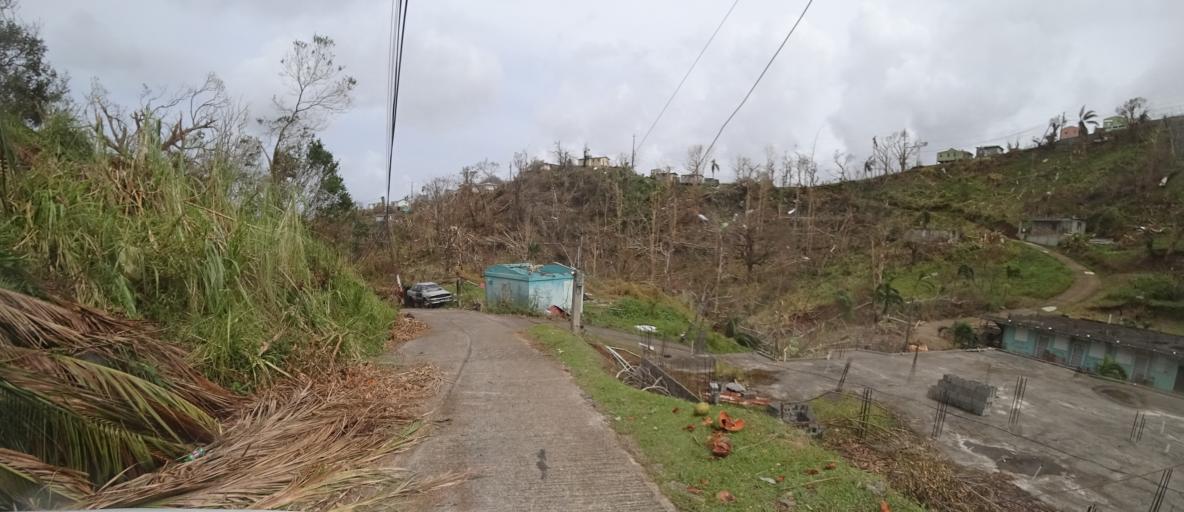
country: DM
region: Saint Andrew
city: Calibishie
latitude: 15.5894
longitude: -61.4053
